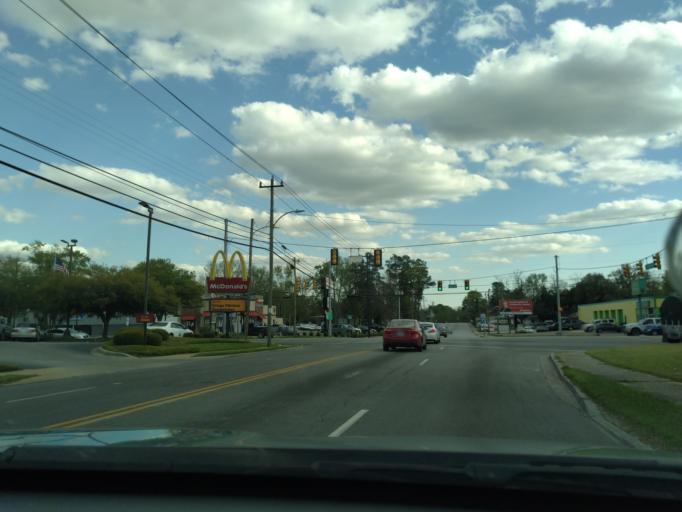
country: US
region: South Carolina
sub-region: Williamsburg County
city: Kingstree
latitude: 33.6636
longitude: -79.8336
